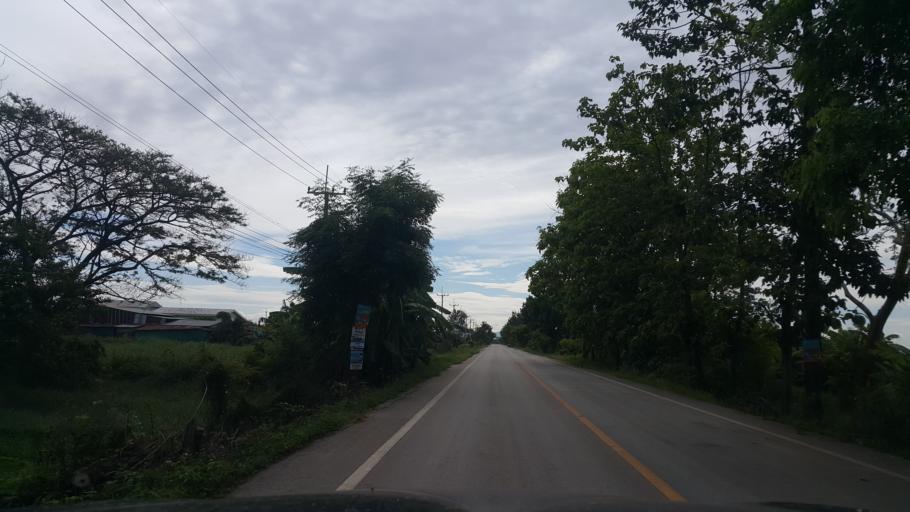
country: TH
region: Uttaradit
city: Phichai
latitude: 17.2849
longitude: 100.0212
